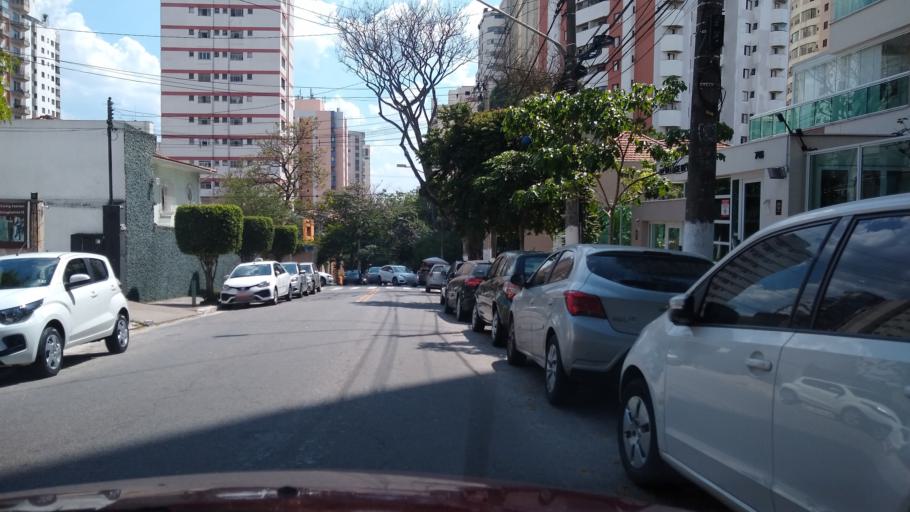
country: BR
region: Sao Paulo
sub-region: Diadema
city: Diadema
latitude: -23.6463
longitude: -46.6648
